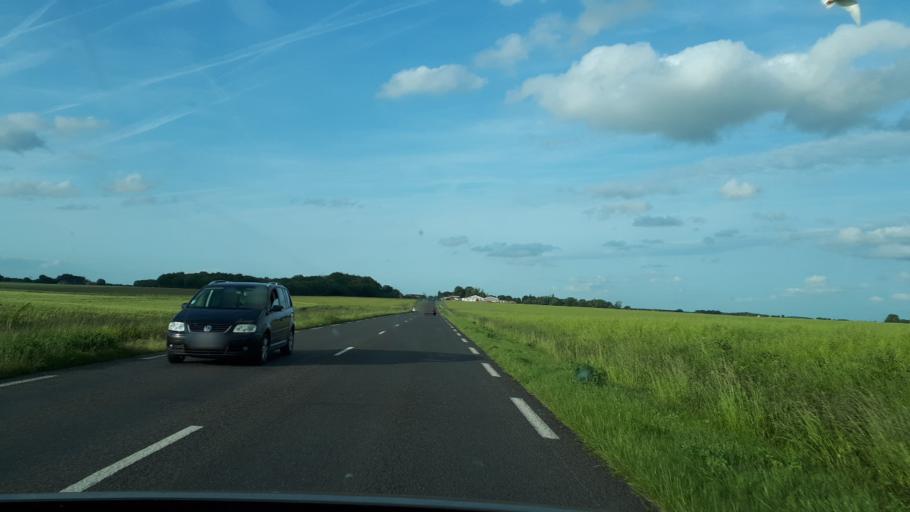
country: FR
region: Centre
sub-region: Departement d'Indre-et-Loire
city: Monnaie
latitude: 47.5255
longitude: 0.8286
